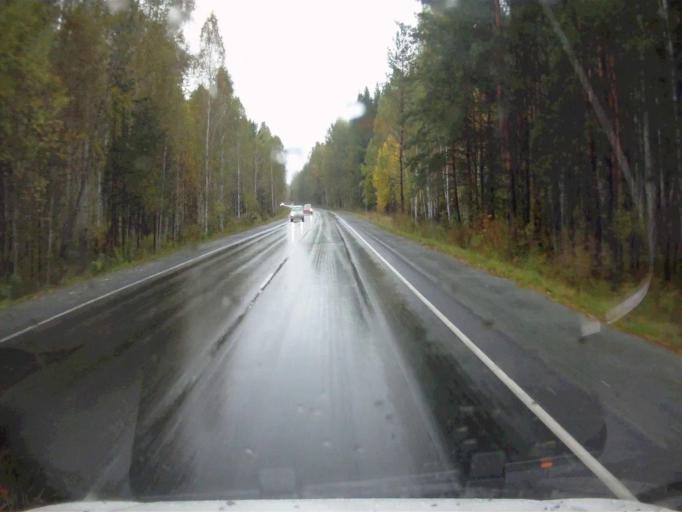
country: RU
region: Chelyabinsk
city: Tayginka
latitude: 55.5926
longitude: 60.6252
